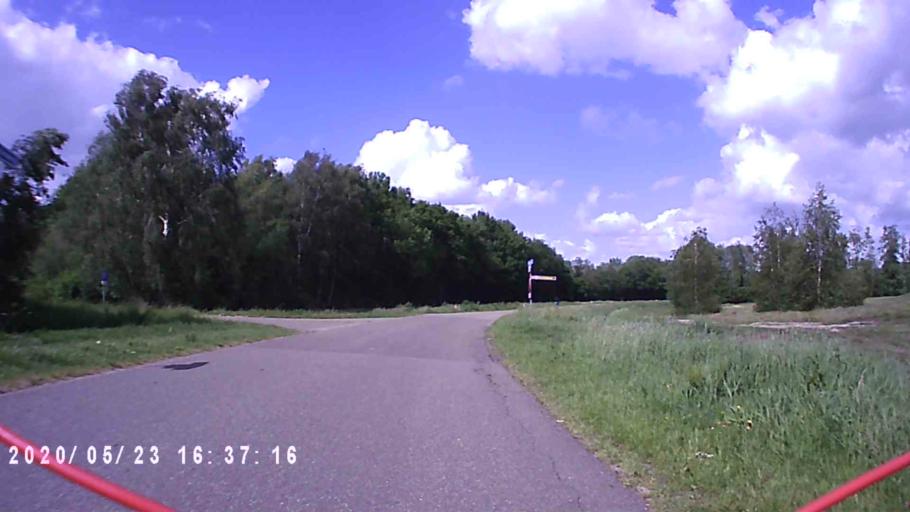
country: NL
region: Groningen
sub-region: Gemeente Slochteren
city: Slochteren
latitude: 53.2638
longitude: 6.8312
